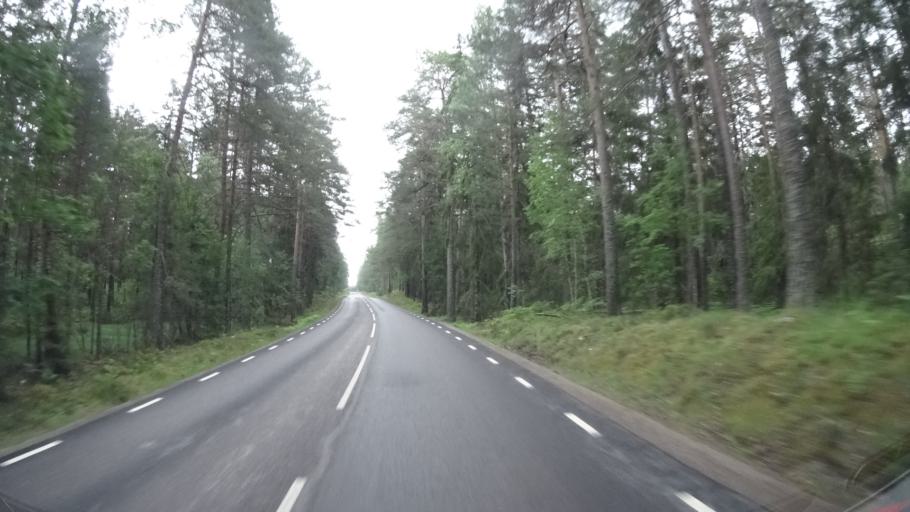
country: SE
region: Kalmar
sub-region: Oskarshamns Kommun
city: Oskarshamn
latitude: 57.3775
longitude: 16.2233
